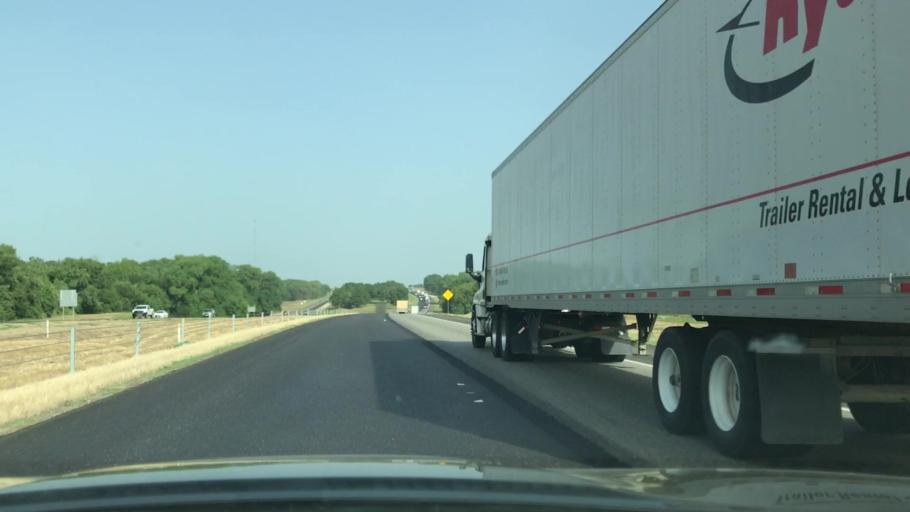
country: US
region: Texas
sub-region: Van Zandt County
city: Wills Point
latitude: 32.6601
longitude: -96.1120
